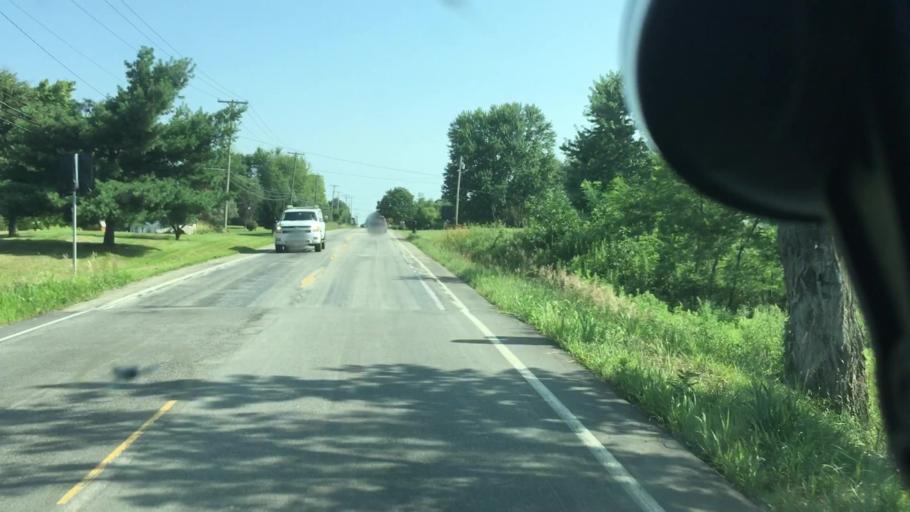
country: US
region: Pennsylvania
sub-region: Lawrence County
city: New Castle
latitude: 41.0090
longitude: -80.2698
